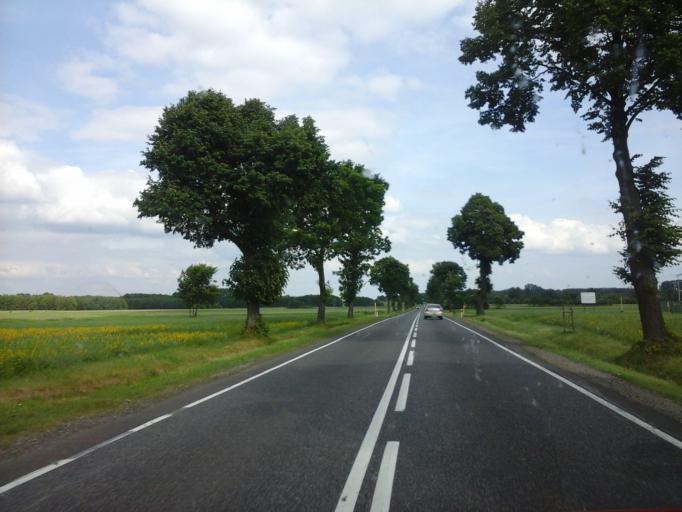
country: PL
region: Lodz Voivodeship
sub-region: Powiat opoczynski
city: Mniszkow
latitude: 51.3183
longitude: 20.0562
